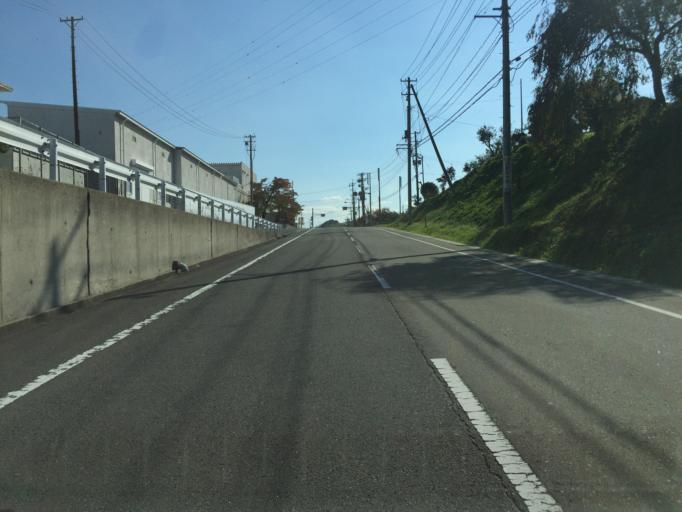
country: JP
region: Fukushima
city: Fukushima-shi
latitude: 37.6988
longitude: 140.4615
